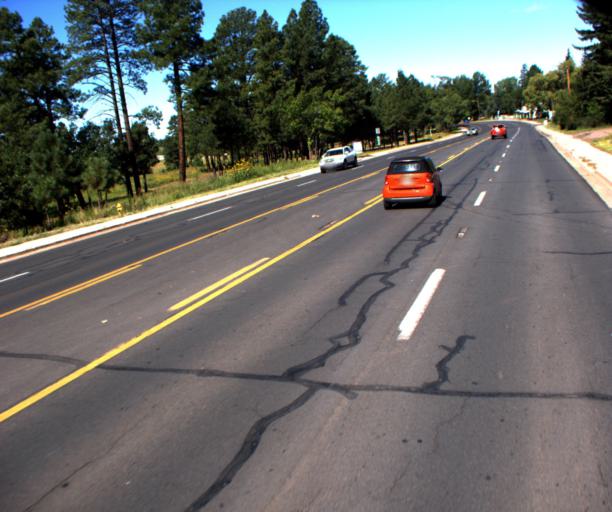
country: US
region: Arizona
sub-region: Navajo County
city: Pinetop-Lakeside
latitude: 34.1251
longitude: -109.9286
